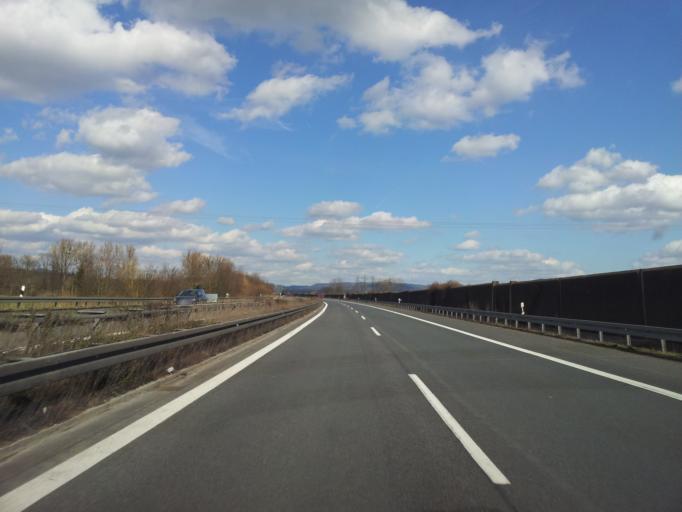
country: DE
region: Bavaria
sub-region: Upper Franconia
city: Memmelsdorf
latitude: 49.9343
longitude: 10.9473
